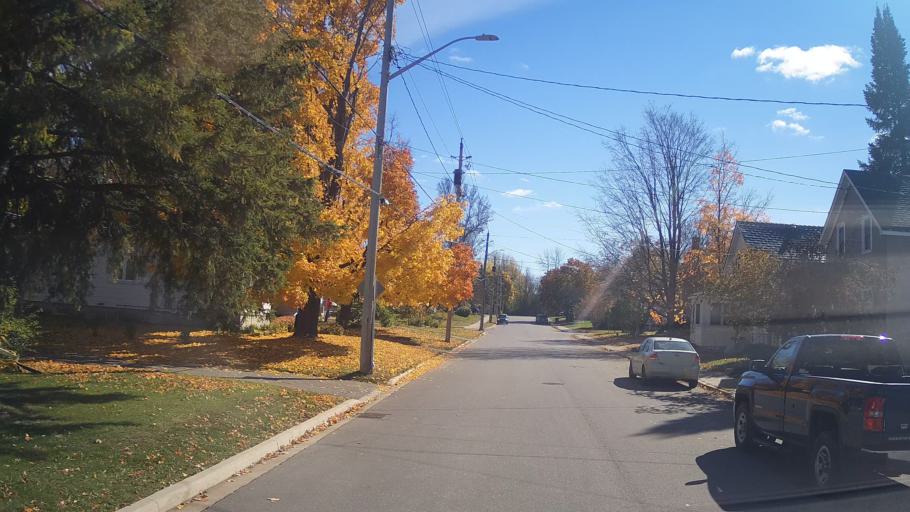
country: CA
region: Ontario
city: Perth
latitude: 44.8956
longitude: -76.2395
